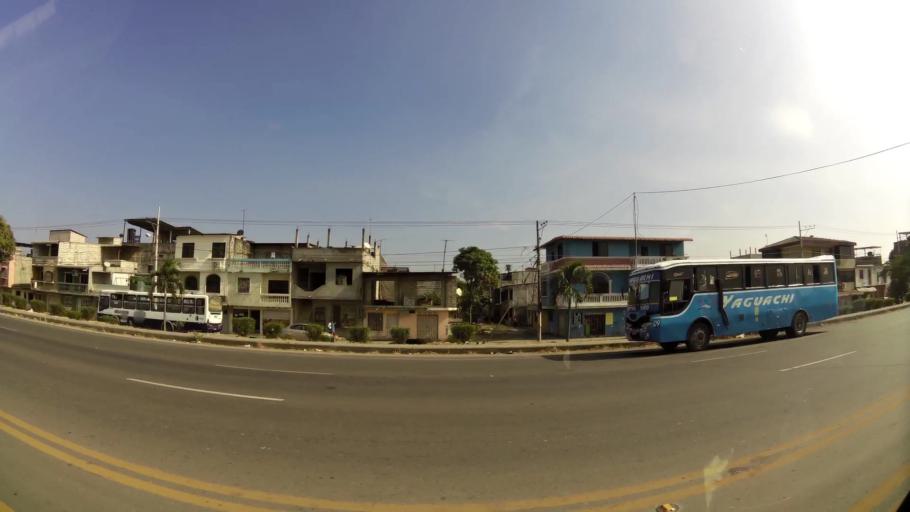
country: EC
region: Guayas
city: Eloy Alfaro
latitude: -2.1663
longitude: -79.7908
